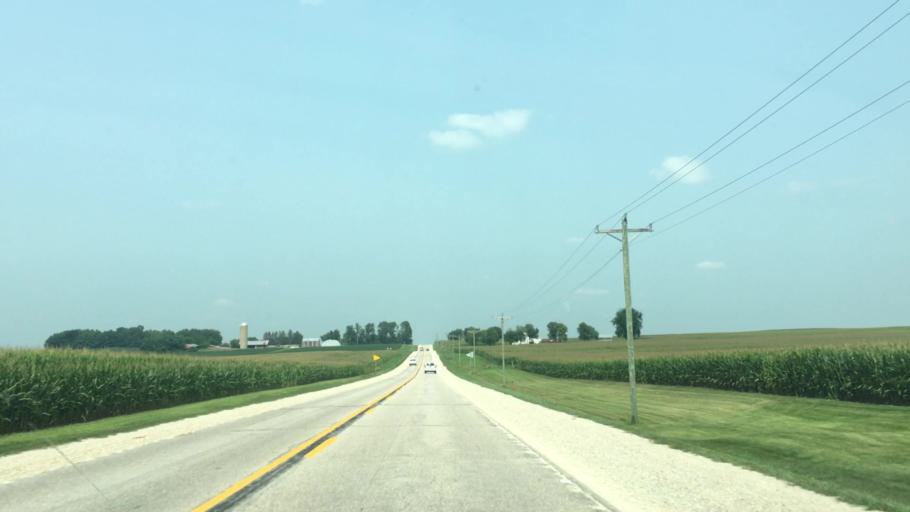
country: US
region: Iowa
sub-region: Benton County
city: Urbana
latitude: 42.3308
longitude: -91.8894
